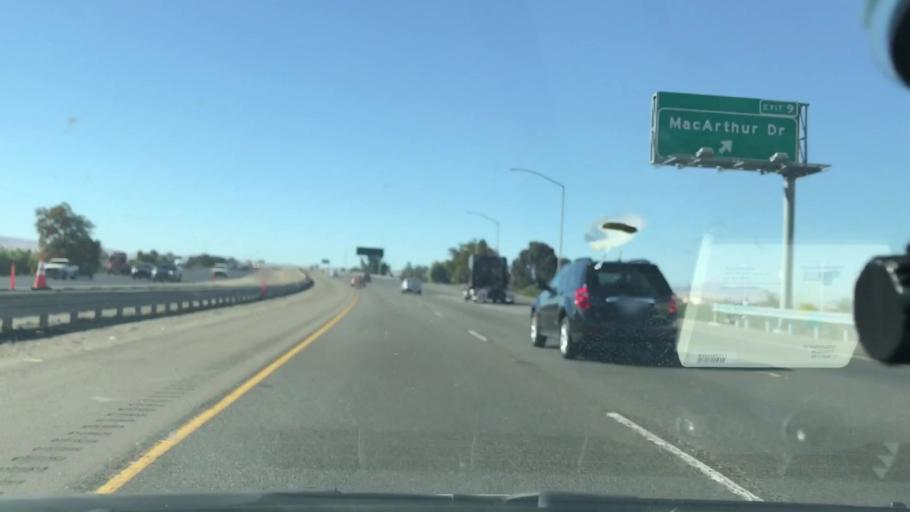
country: US
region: California
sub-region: San Joaquin County
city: Tracy
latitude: 37.7654
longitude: -121.4103
